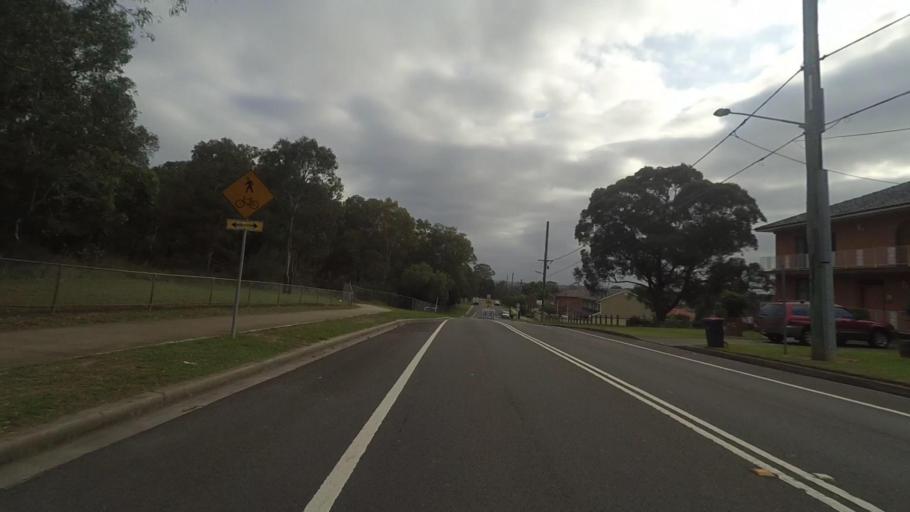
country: AU
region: New South Wales
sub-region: Bankstown
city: Regents Park
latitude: -33.9069
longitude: 150.9925
